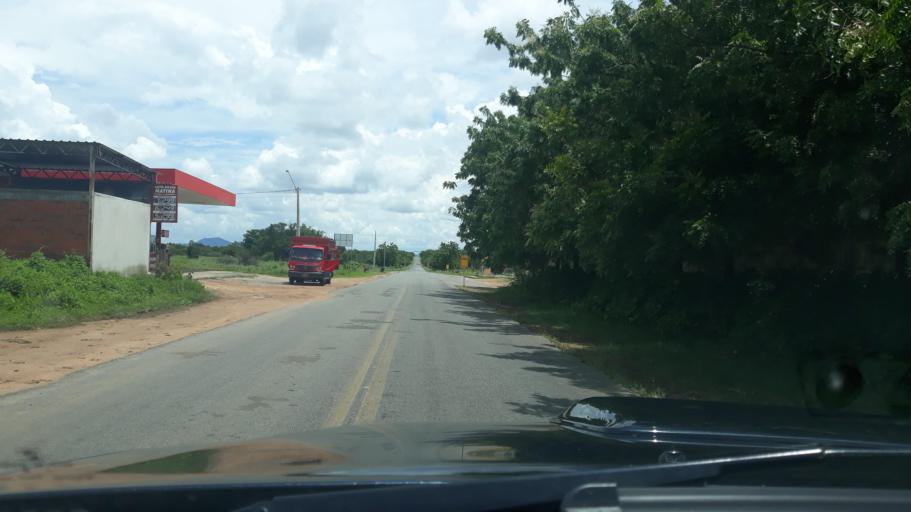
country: BR
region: Bahia
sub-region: Guanambi
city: Guanambi
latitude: -13.9161
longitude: -42.8444
